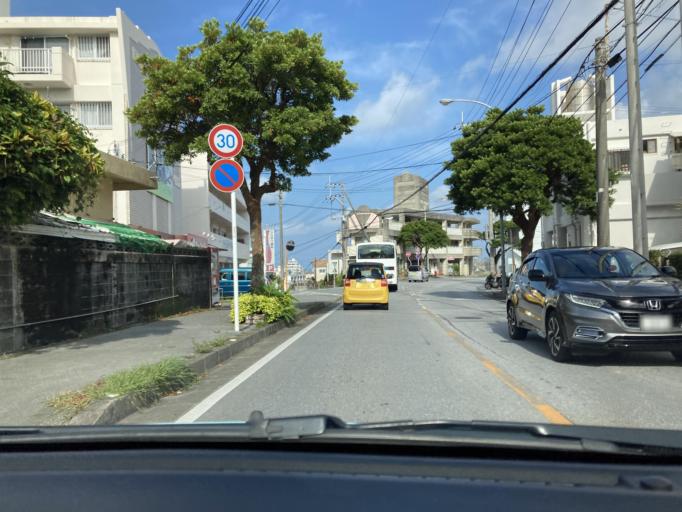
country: JP
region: Okinawa
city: Ginowan
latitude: 26.2595
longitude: 127.7645
